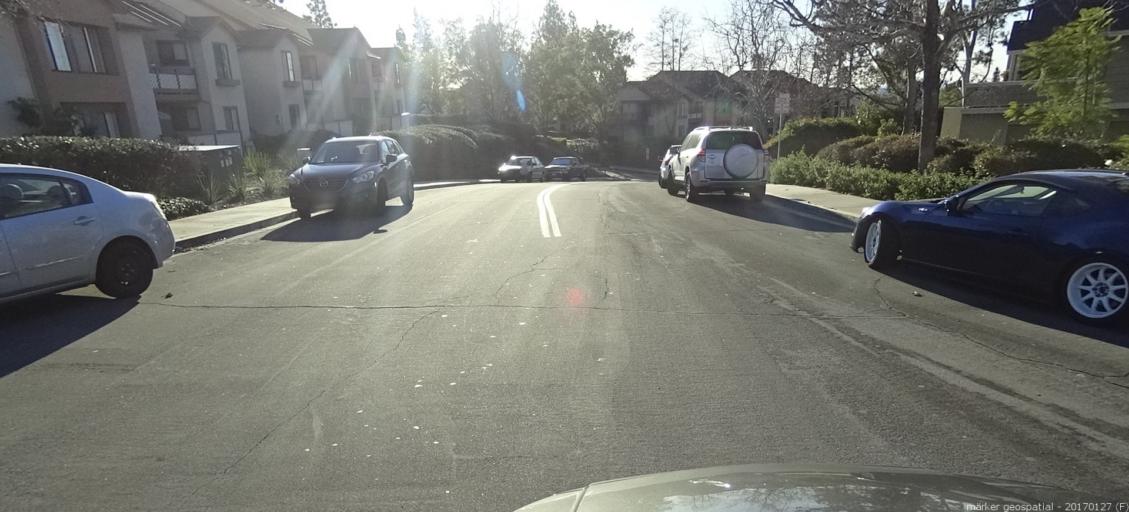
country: US
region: California
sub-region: Orange County
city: Lake Forest
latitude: 33.6565
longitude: -117.6706
